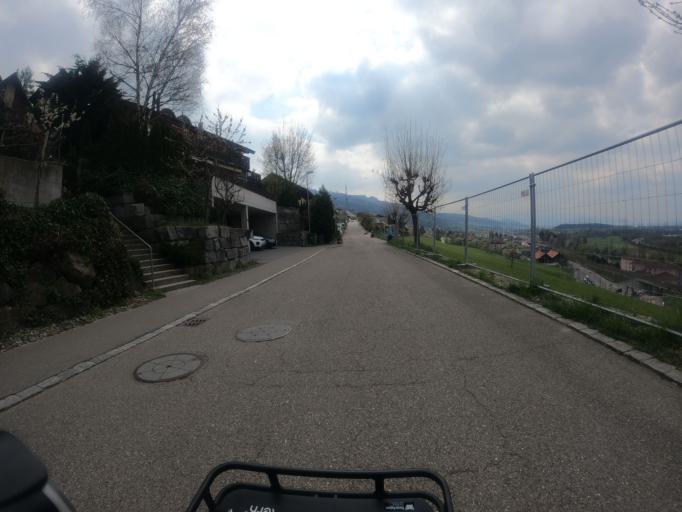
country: CH
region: Lucerne
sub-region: Lucerne-Land District
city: Root
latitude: 47.1250
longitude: 8.3994
